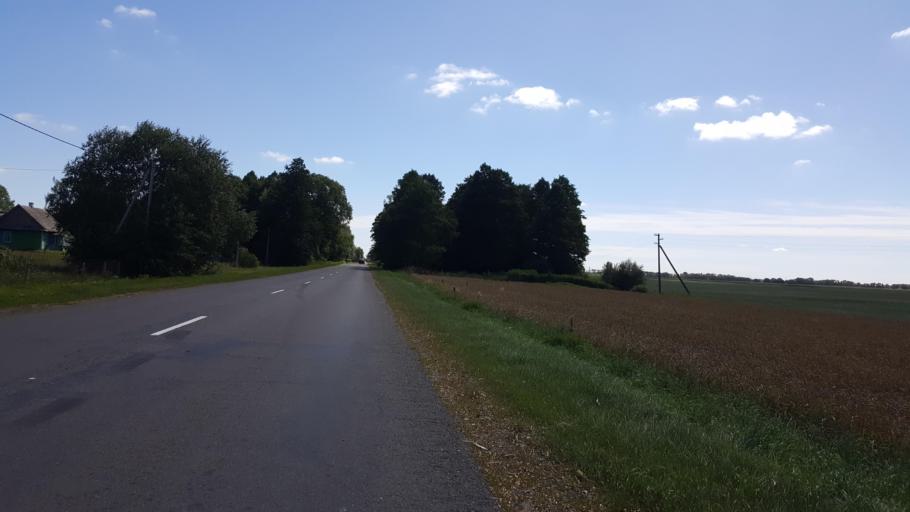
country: BY
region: Brest
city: Kobryn
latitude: 52.3456
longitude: 24.2167
